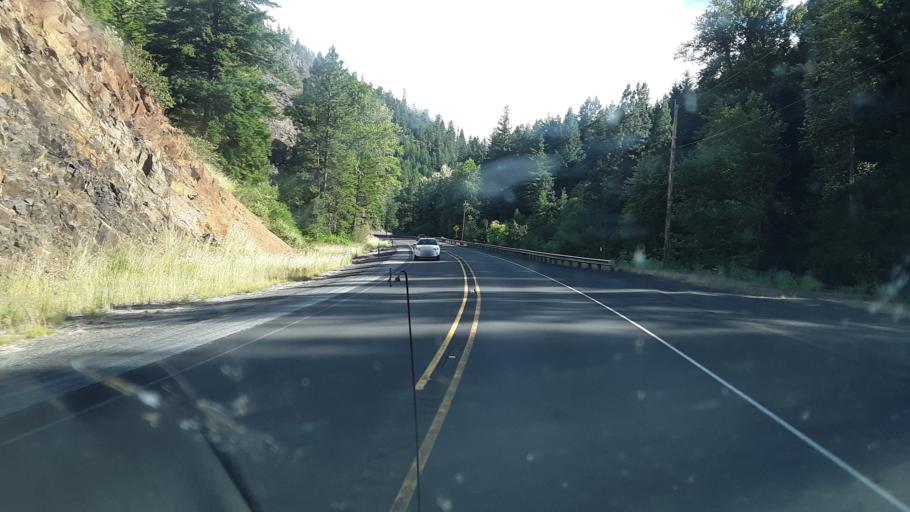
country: US
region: Washington
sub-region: Kittitas County
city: Cle Elum
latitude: 47.2302
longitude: -120.6961
